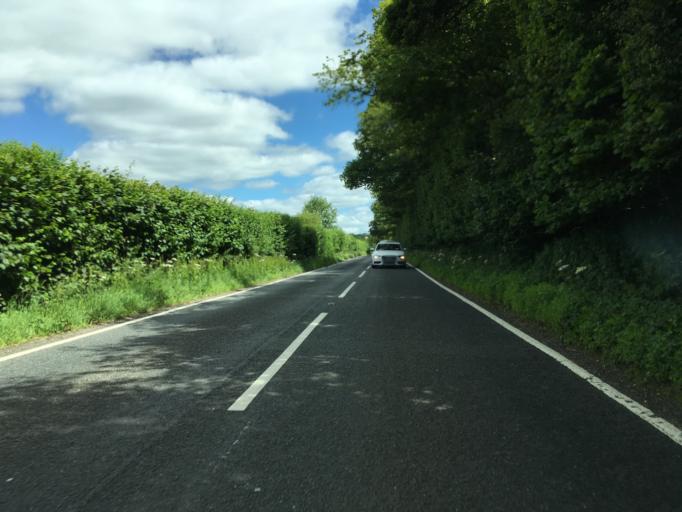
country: GB
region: England
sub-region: Hampshire
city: Highclere
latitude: 51.2944
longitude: -1.4163
